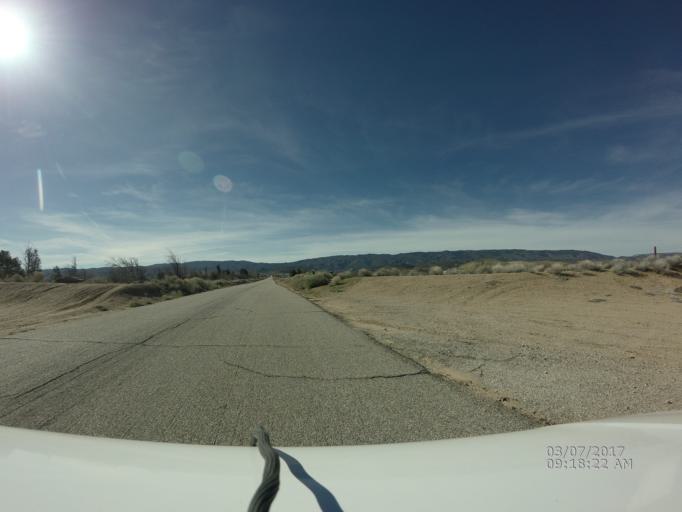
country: US
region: California
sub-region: Los Angeles County
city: Green Valley
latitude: 34.7877
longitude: -118.5900
